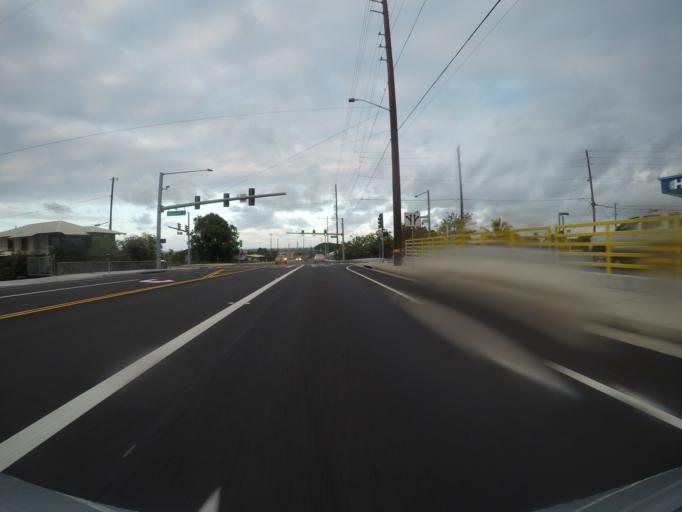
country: US
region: Hawaii
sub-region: Hawaii County
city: Hilo
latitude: 19.6837
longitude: -155.0823
